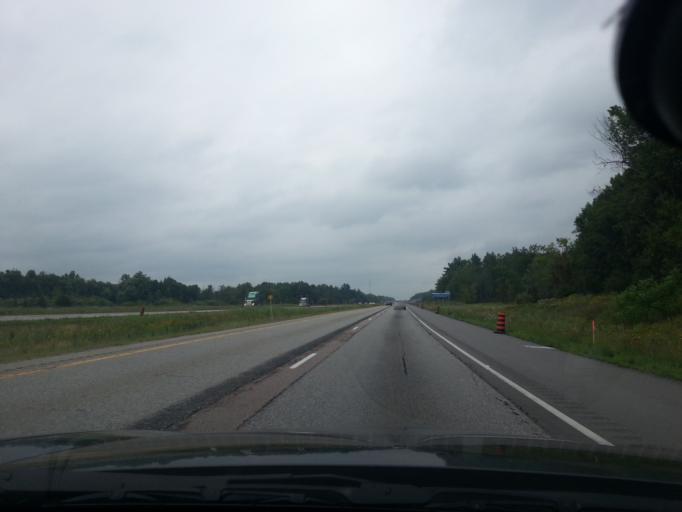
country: US
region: New York
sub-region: Jefferson County
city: Alexandria Bay
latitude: 44.4521
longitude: -75.8872
